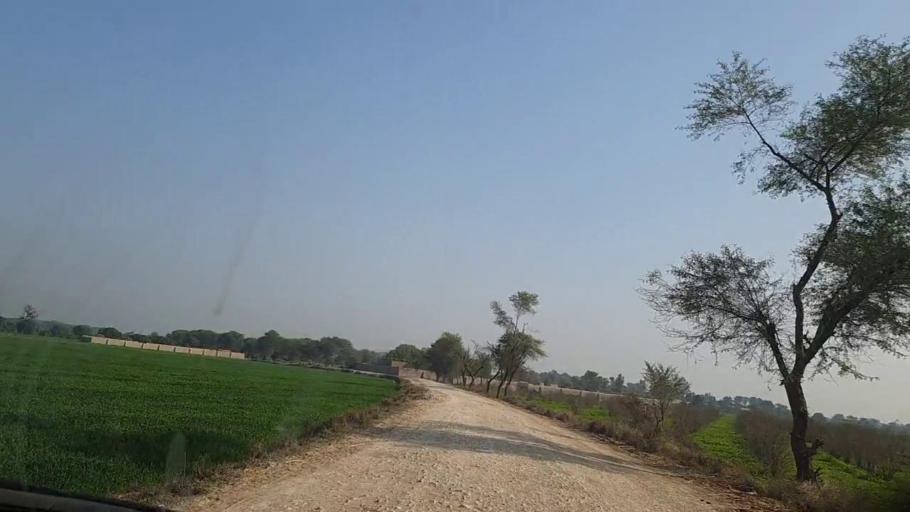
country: PK
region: Sindh
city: Moro
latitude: 26.8146
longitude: 67.9580
